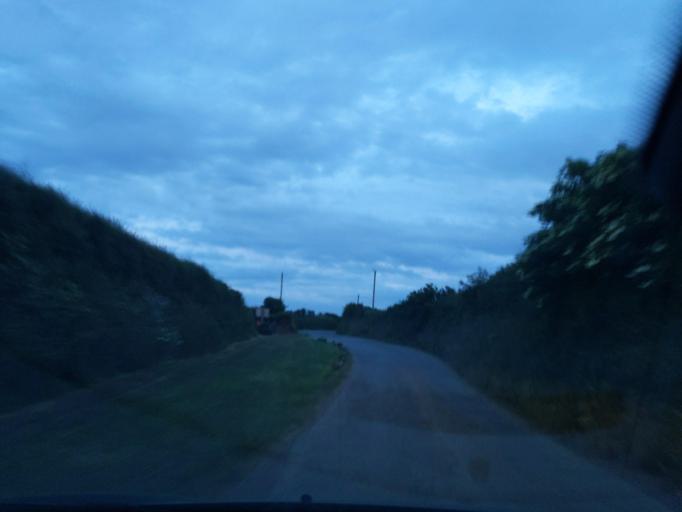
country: GB
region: England
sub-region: Cornwall
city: Wadebridge
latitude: 50.5764
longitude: -4.8304
